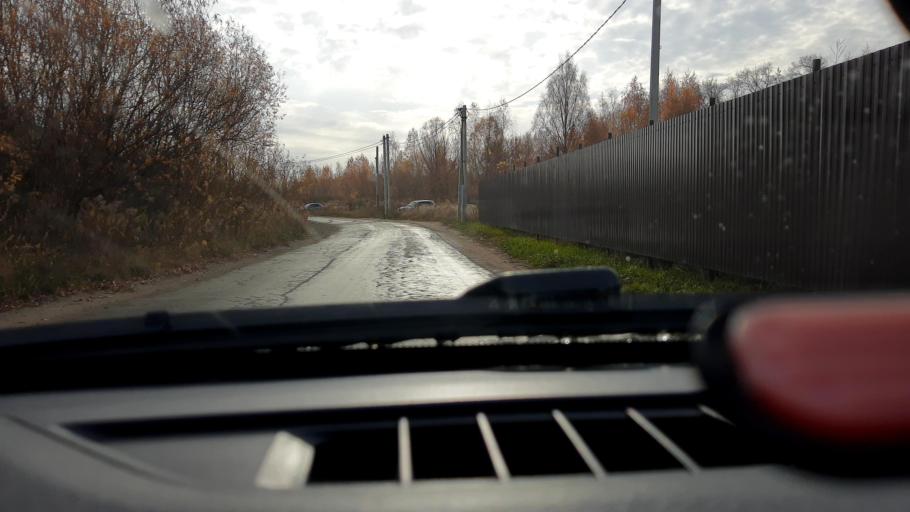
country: RU
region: Nizjnij Novgorod
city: Gorbatovka
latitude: 56.3173
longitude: 43.8463
